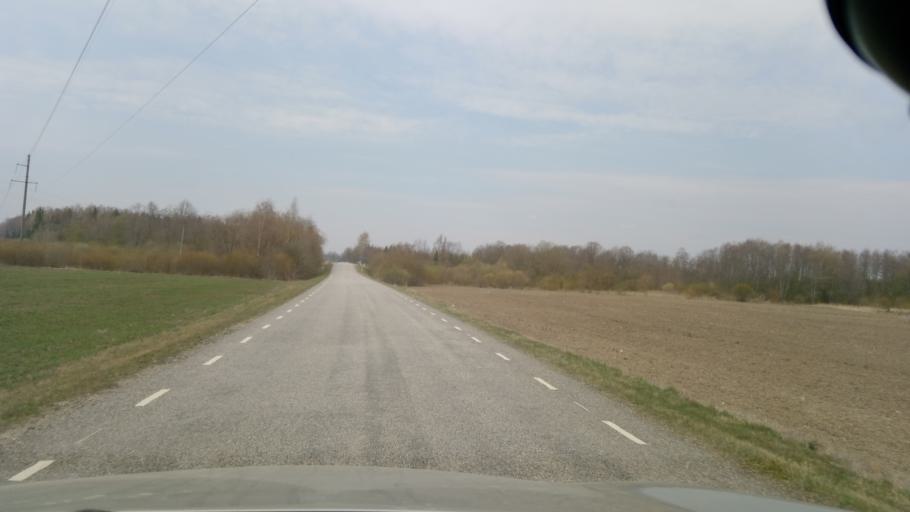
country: EE
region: Jaervamaa
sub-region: Tueri vald
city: Tueri
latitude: 58.7976
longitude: 25.4787
